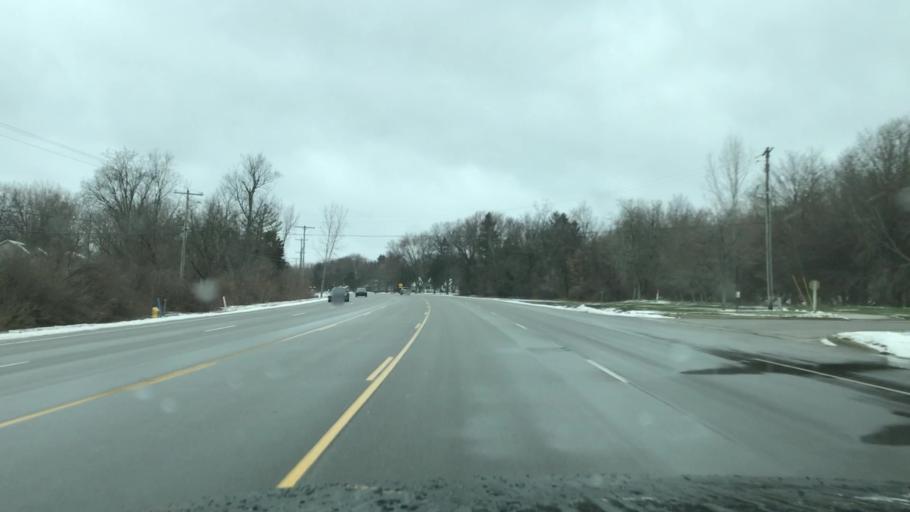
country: US
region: Michigan
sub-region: Kent County
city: Forest Hills
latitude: 42.9225
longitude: -85.5066
